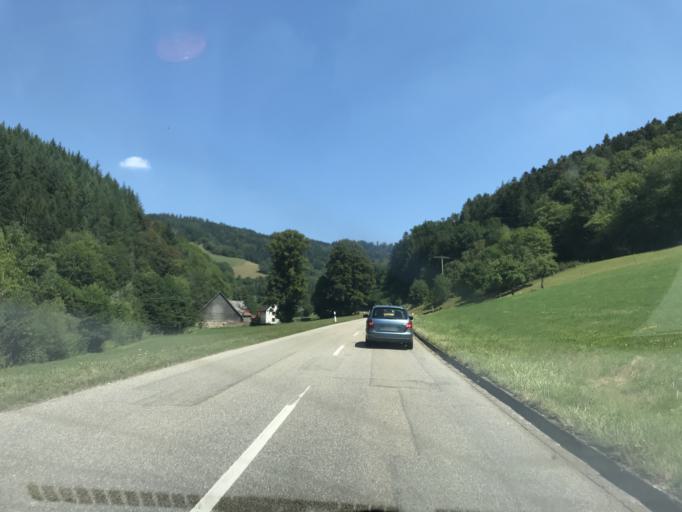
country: DE
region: Baden-Wuerttemberg
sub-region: Freiburg Region
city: Sankt Peter
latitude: 48.0051
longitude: 7.9982
